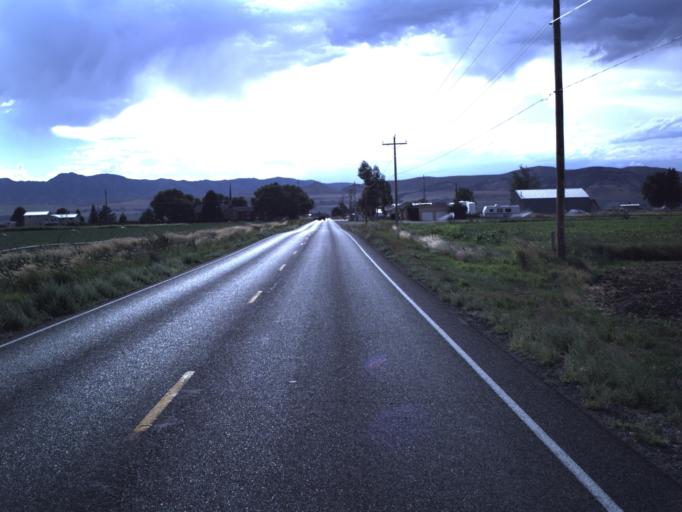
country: US
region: Utah
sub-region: Cache County
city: Lewiston
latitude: 41.9757
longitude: -111.8906
